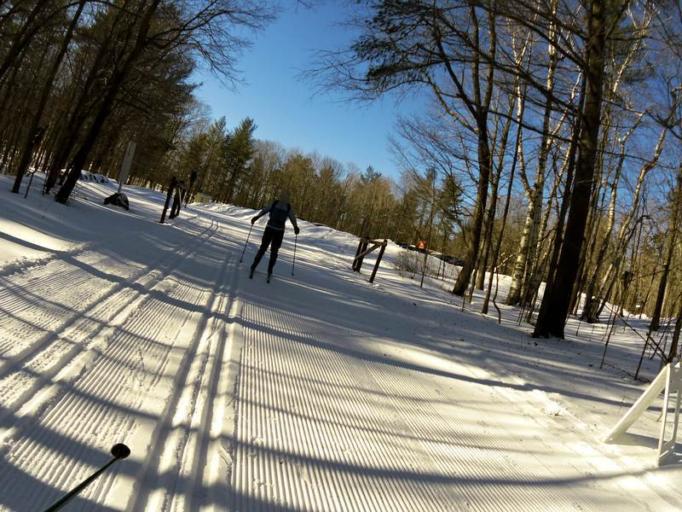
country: CA
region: Quebec
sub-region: Outaouais
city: Gatineau
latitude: 45.4842
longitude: -75.8454
